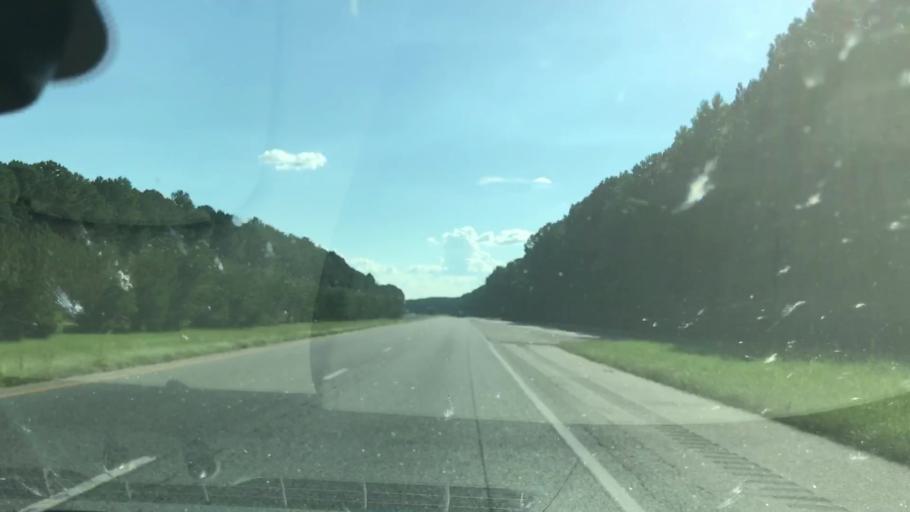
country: US
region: Georgia
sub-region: Harris County
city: Pine Mountain
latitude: 32.8548
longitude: -84.9826
